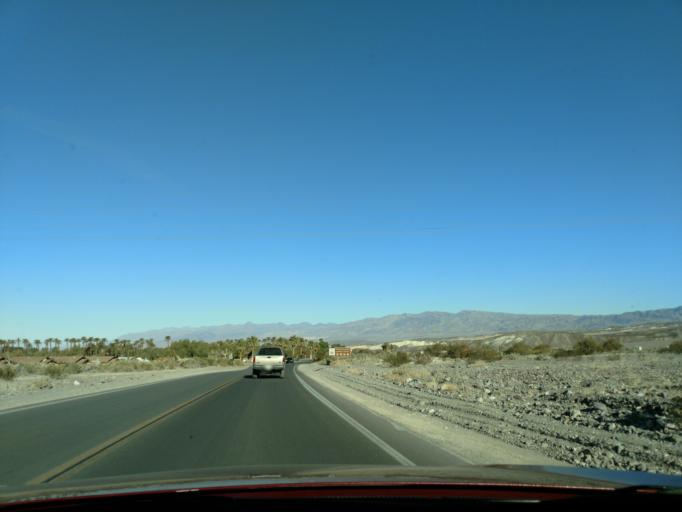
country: US
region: Nevada
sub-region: Nye County
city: Beatty
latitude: 36.4545
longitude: -116.8646
